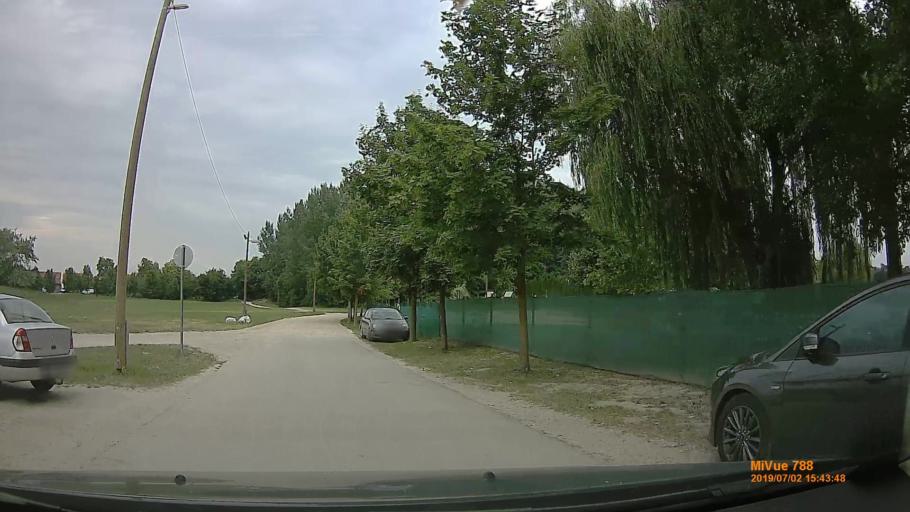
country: HU
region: Gyor-Moson-Sopron
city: Mosonmagyarovar
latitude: 47.8743
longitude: 17.2910
